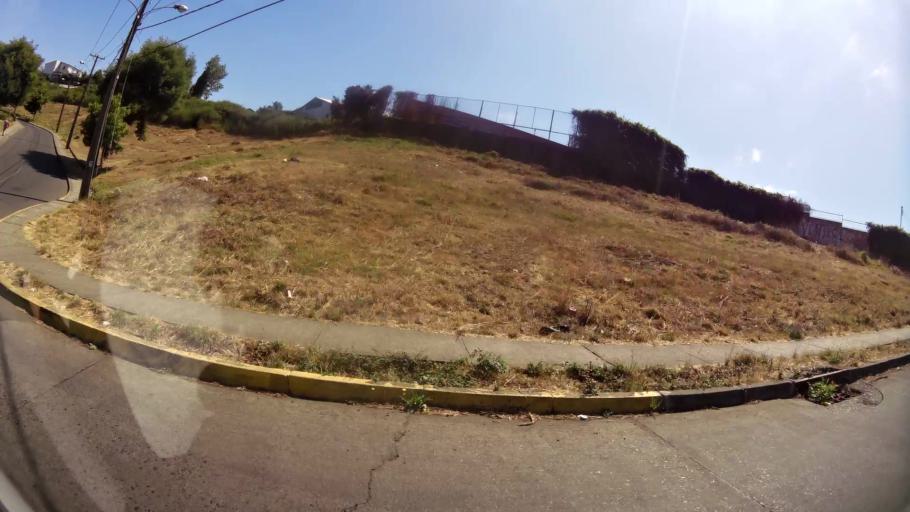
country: CL
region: Biobio
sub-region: Provincia de Concepcion
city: Concepcion
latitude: -36.7904
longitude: -73.0420
